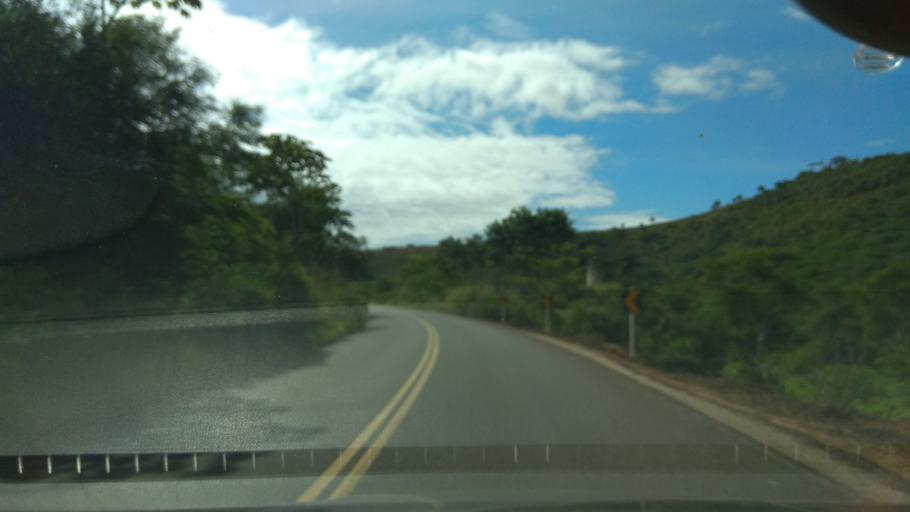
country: BR
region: Bahia
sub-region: Ubaira
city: Ubaira
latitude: -13.2630
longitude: -39.6793
